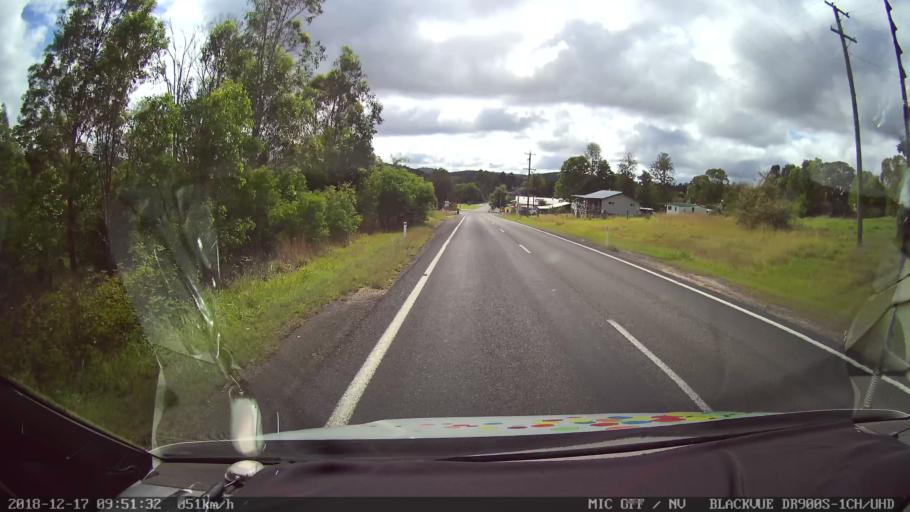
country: AU
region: New South Wales
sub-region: Tenterfield Municipality
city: Carrolls Creek
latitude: -28.9266
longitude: 152.3744
